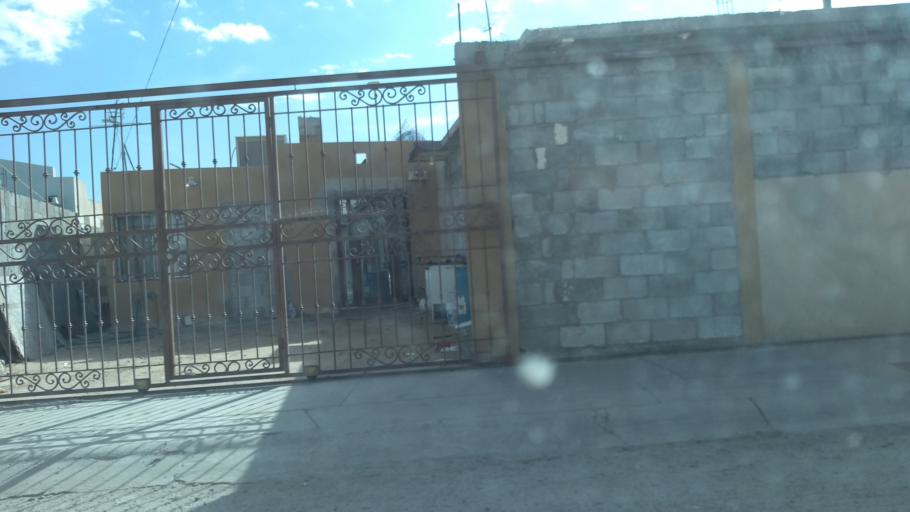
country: US
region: Texas
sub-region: El Paso County
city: San Elizario
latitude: 31.5831
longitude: -106.3542
